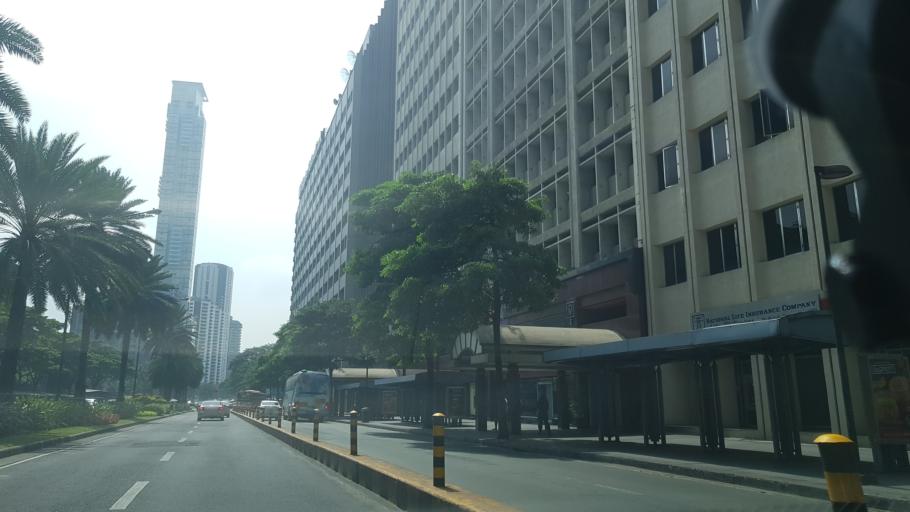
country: PH
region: Metro Manila
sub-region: Makati City
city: Makati City
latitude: 14.5562
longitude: 121.0222
